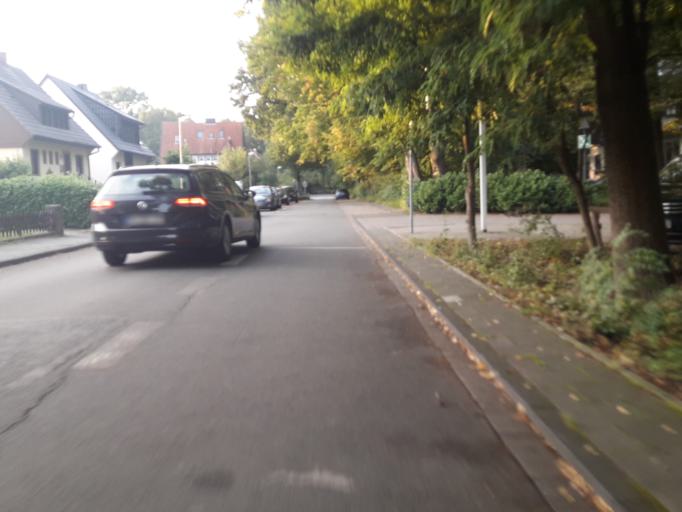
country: DE
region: North Rhine-Westphalia
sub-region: Regierungsbezirk Munster
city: Muenster
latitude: 51.9275
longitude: 7.6573
